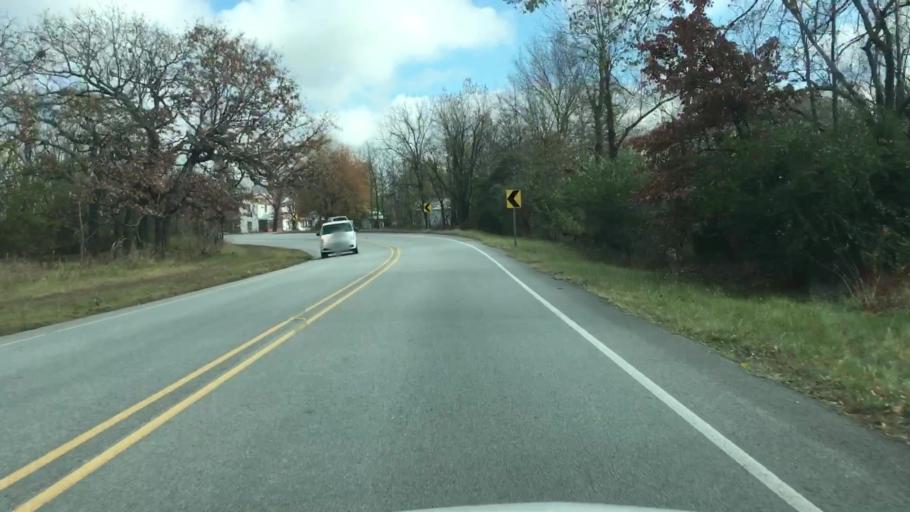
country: US
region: Arkansas
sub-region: Benton County
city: Centerton
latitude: 36.2941
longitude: -94.3434
